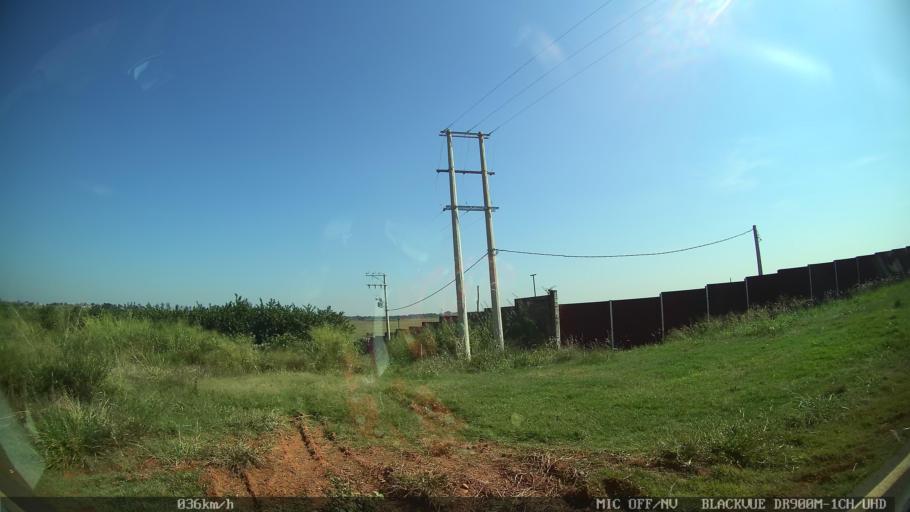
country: BR
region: Sao Paulo
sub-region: Valinhos
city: Valinhos
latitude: -23.0196
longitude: -47.0872
